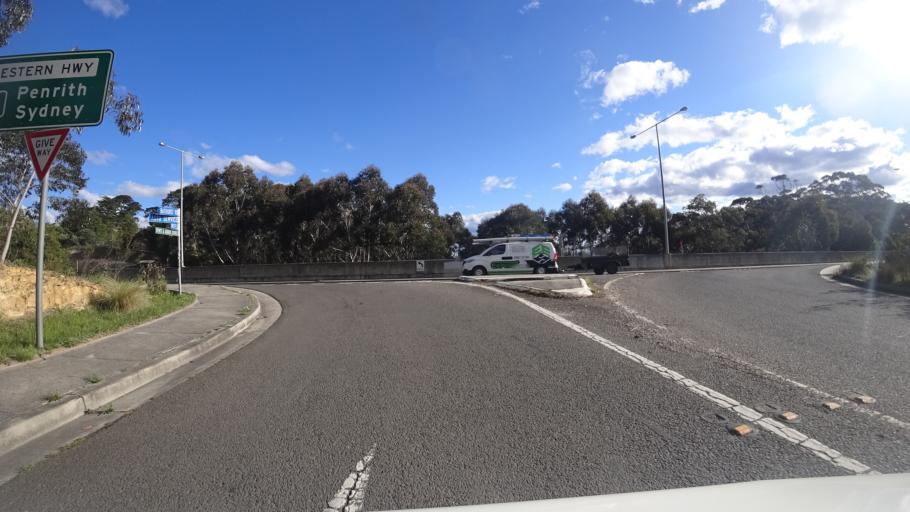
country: AU
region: New South Wales
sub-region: Blue Mountains Municipality
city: Katoomba
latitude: -33.7063
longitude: 150.2991
